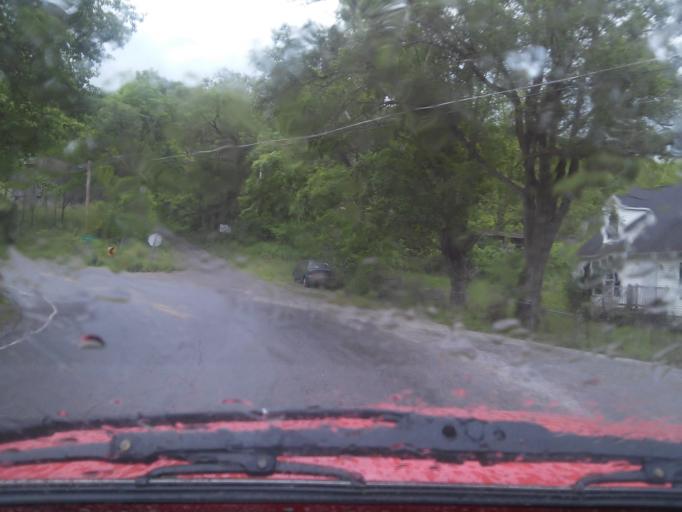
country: US
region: Virginia
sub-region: Montgomery County
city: Blacksburg
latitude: 37.3845
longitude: -80.3618
